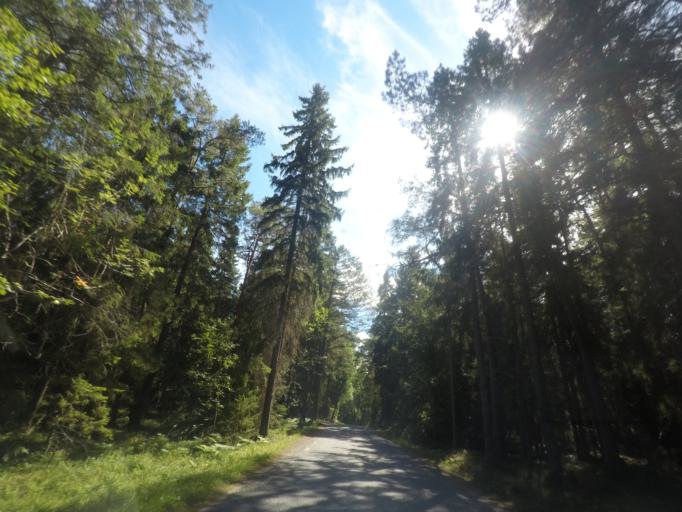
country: SE
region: Stockholm
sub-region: Norrtalje Kommun
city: Arno
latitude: 60.1976
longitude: 18.7388
